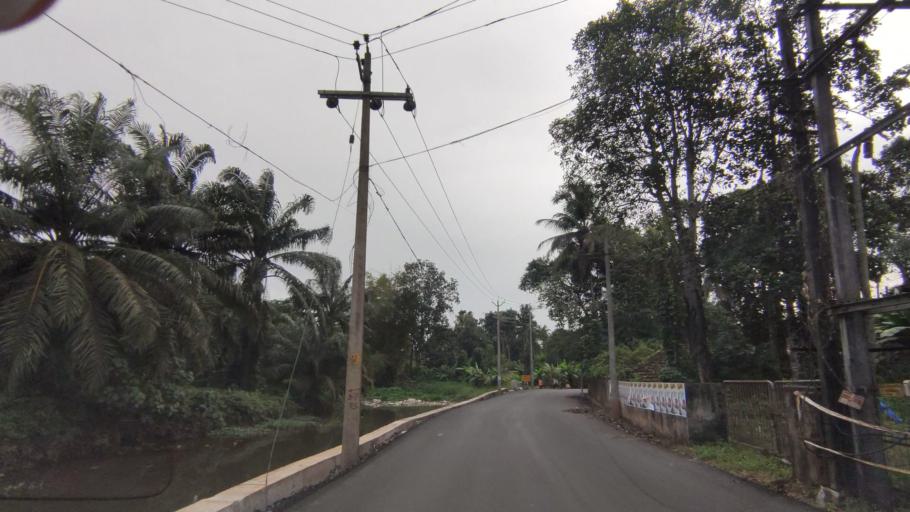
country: IN
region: Kerala
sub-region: Kottayam
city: Kottayam
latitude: 9.6660
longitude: 76.5300
